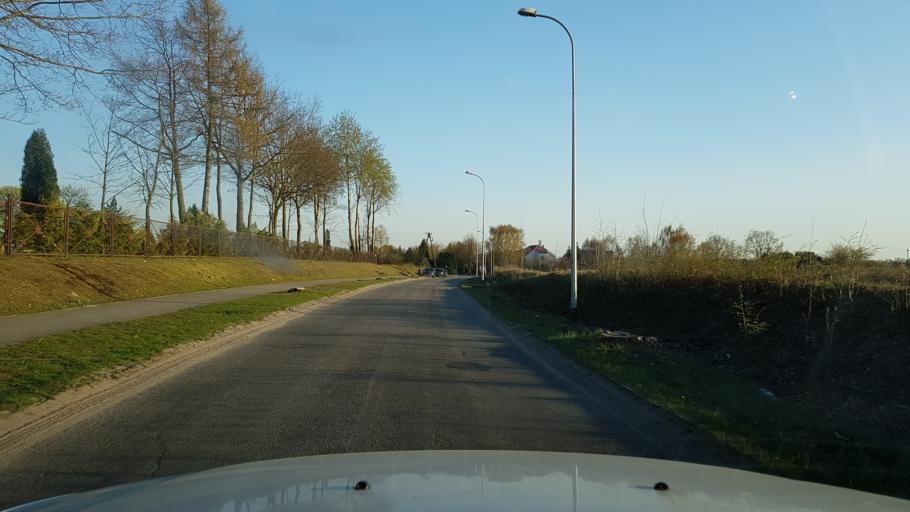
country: PL
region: West Pomeranian Voivodeship
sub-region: Powiat bialogardzki
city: Bialogard
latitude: 54.0221
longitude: 15.9878
